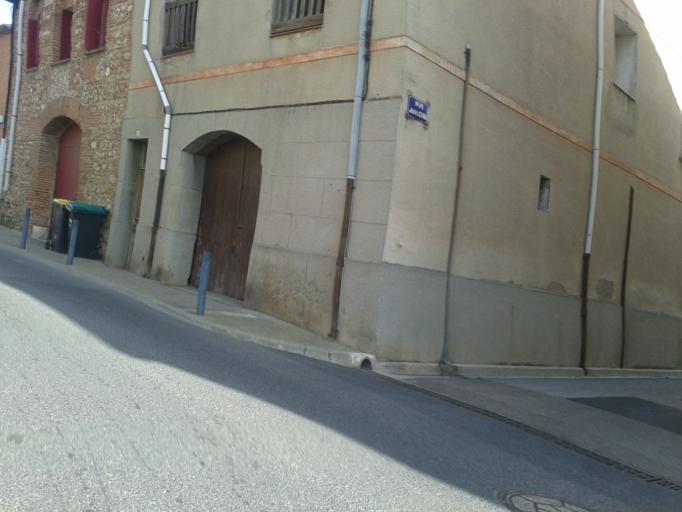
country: FR
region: Languedoc-Roussillon
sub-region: Departement des Pyrenees-Orientales
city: Pezilla-la-Riviere
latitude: 42.6944
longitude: 2.7734
